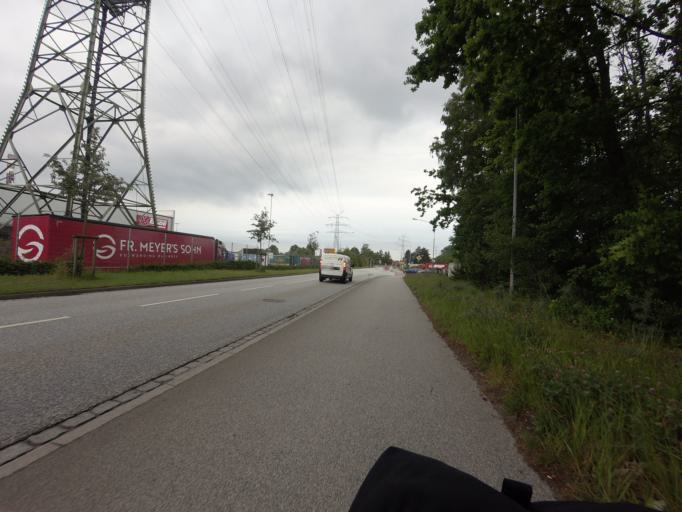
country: DE
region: Schleswig-Holstein
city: Ratekau
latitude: 53.9027
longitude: 10.7798
